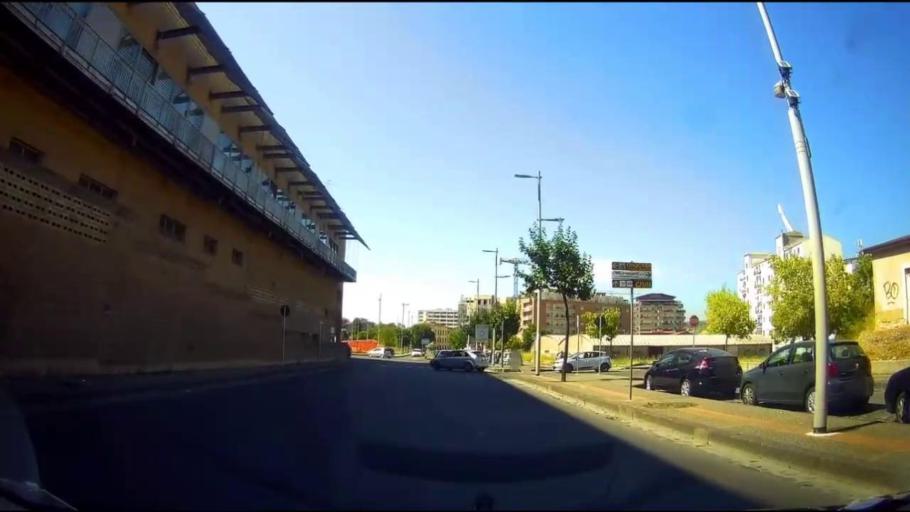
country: IT
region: Calabria
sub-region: Provincia di Cosenza
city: Cosenza
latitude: 39.2955
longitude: 16.2575
